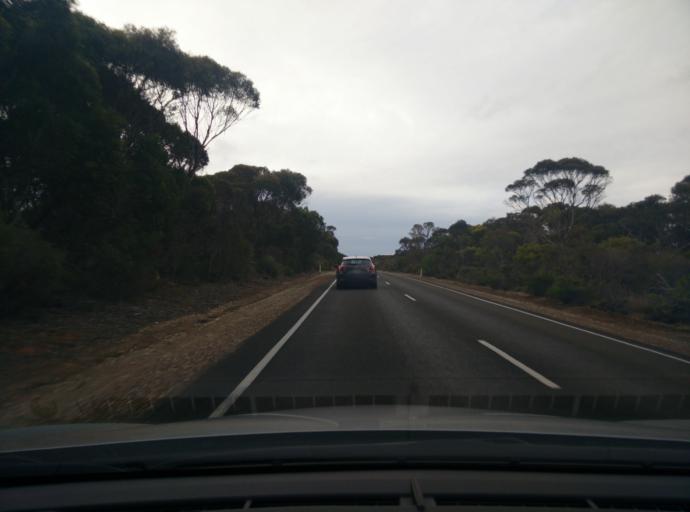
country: AU
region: South Australia
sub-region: Kangaroo Island
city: Kingscote
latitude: -35.7963
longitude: 137.6602
